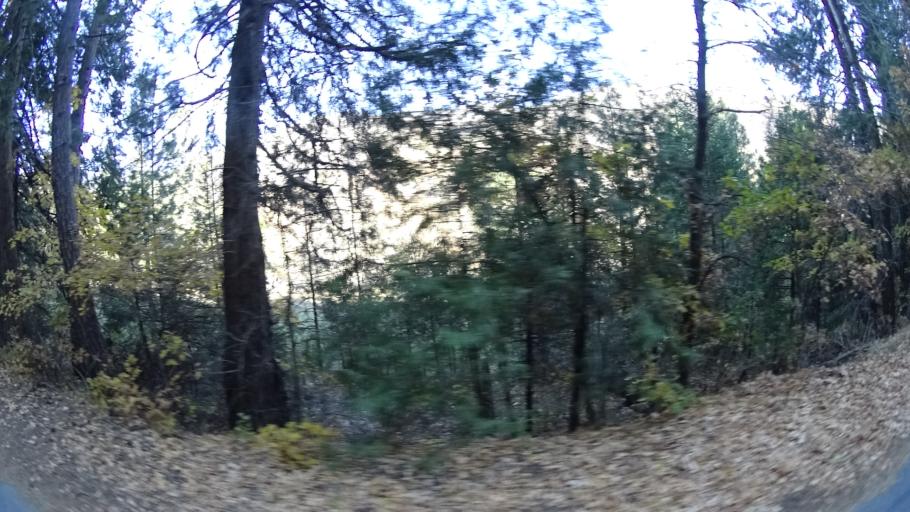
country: US
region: California
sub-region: Siskiyou County
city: Yreka
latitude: 41.8400
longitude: -122.8770
